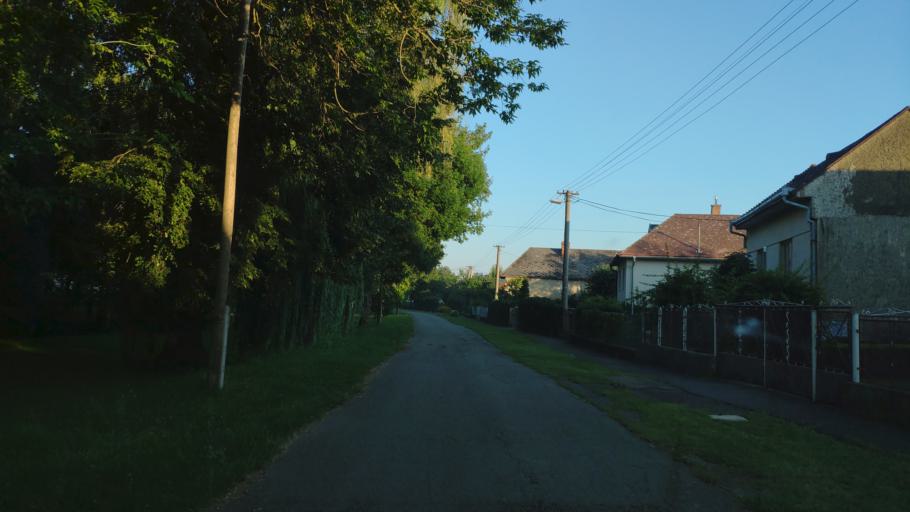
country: SK
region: Kosicky
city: Secovce
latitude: 48.7636
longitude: 21.6580
